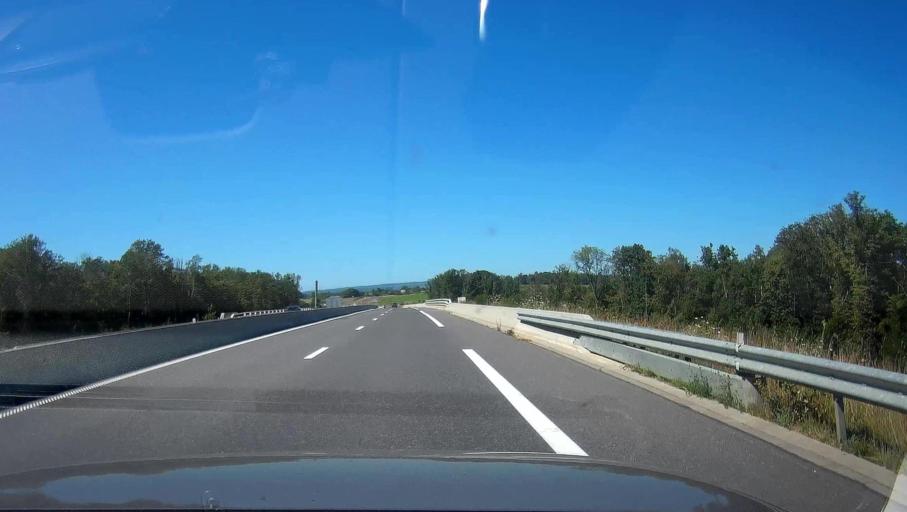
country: FR
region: Champagne-Ardenne
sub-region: Departement des Ardennes
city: Warcq
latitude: 49.7587
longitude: 4.6531
